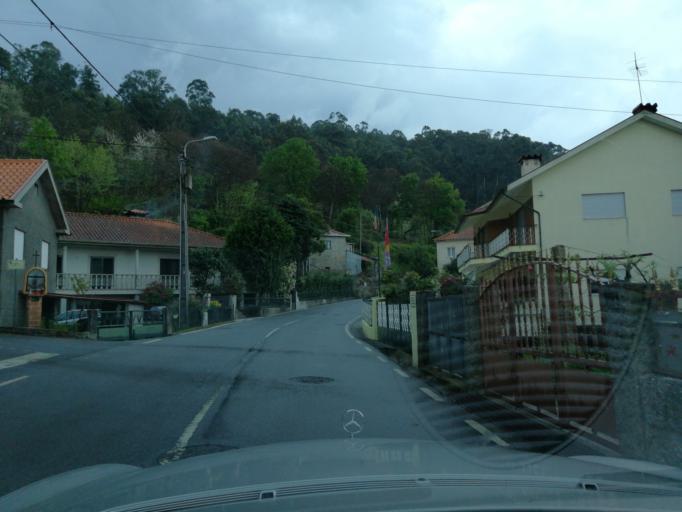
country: PT
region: Braga
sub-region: Braga
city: Oliveira
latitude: 41.4670
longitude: -8.4743
